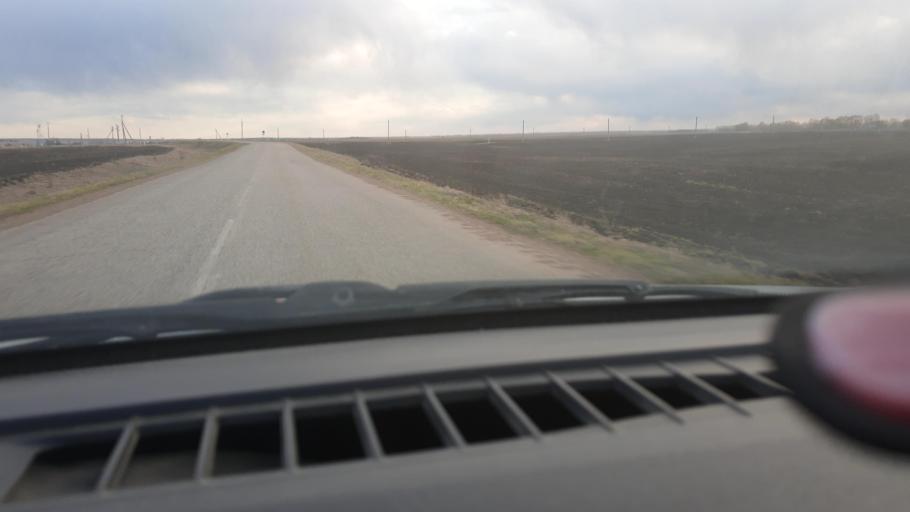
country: RU
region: Bashkortostan
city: Asanovo
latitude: 54.9423
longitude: 55.5186
